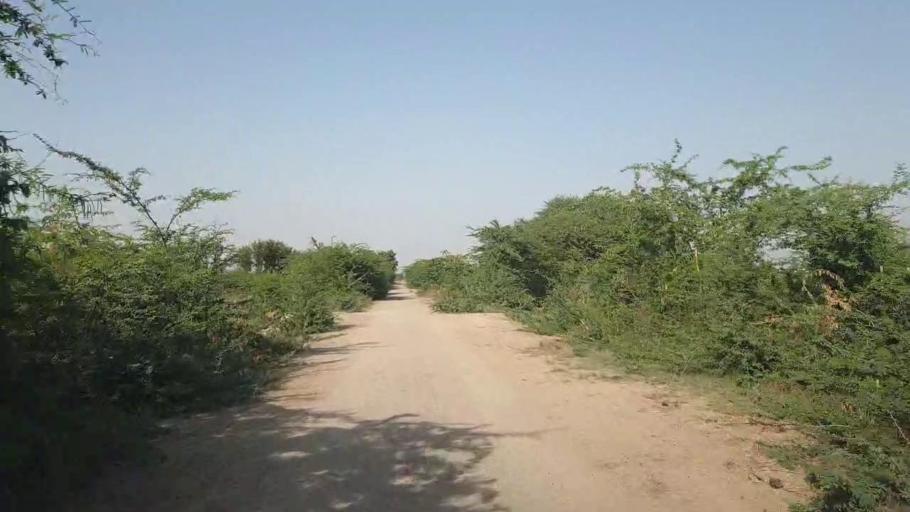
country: PK
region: Sindh
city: Dhoro Naro
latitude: 25.4673
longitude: 69.5391
